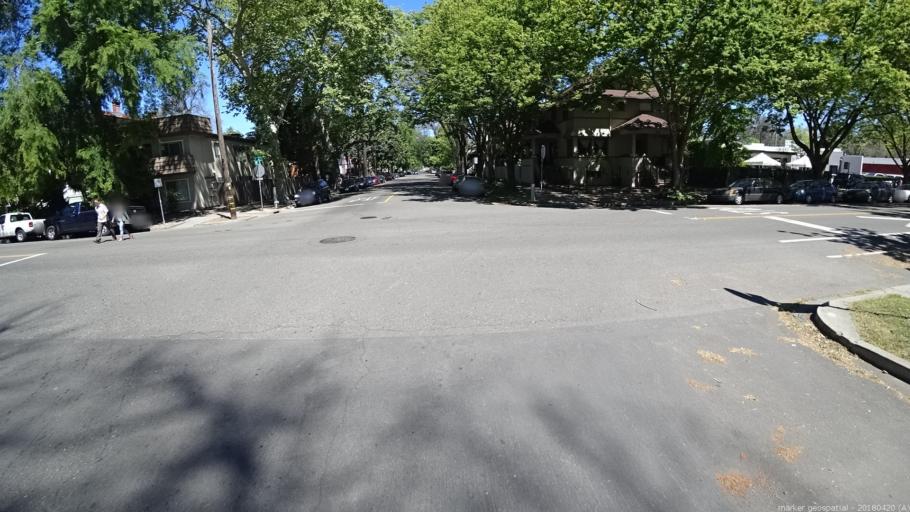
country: US
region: California
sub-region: Sacramento County
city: Sacramento
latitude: 38.5792
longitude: -121.4802
